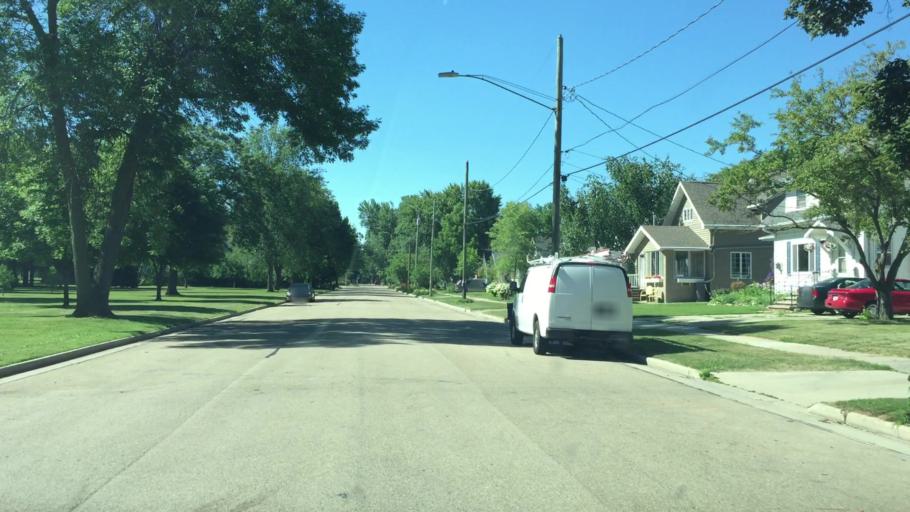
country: US
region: Wisconsin
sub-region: Winnebago County
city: Menasha
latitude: 44.1959
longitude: -88.4420
